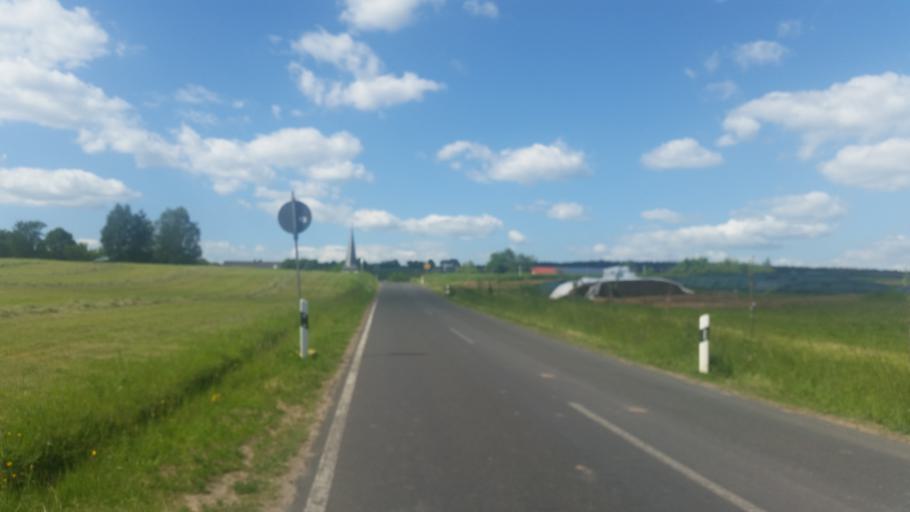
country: DE
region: Bavaria
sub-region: Regierungsbezirk Unterfranken
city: Burgpreppach
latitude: 50.1150
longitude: 10.6730
